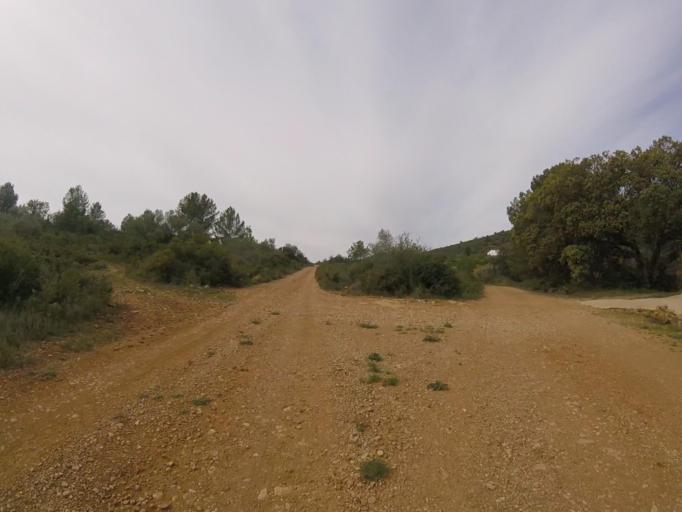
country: ES
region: Valencia
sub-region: Provincia de Castello
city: Cabanes
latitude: 40.1899
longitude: 0.1097
